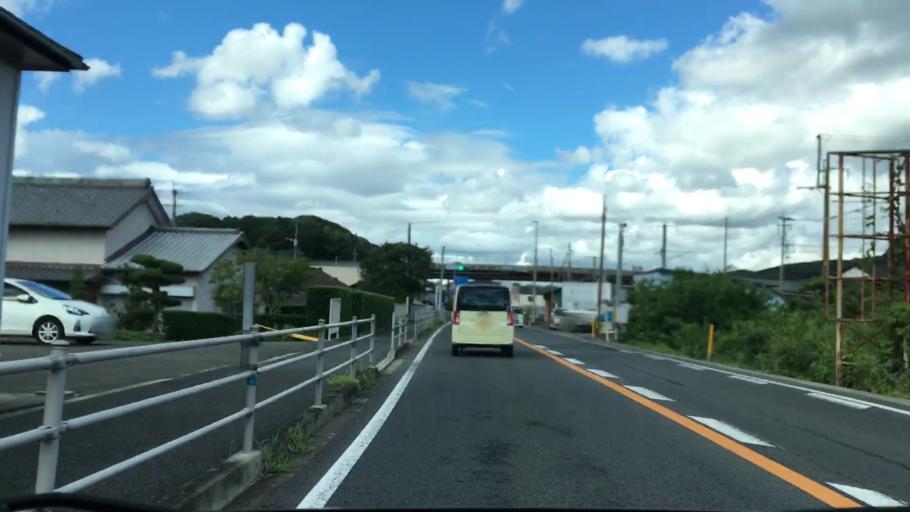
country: JP
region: Nagasaki
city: Sasebo
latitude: 33.1470
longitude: 129.8279
